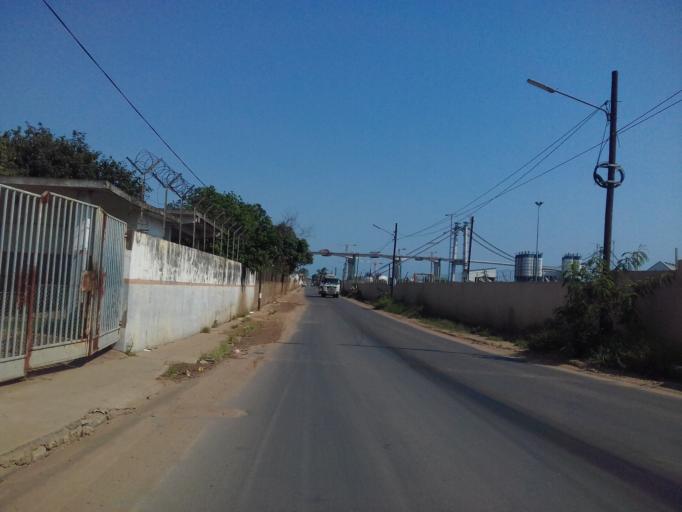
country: MZ
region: Maputo City
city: Maputo
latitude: -25.9584
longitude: 32.5542
